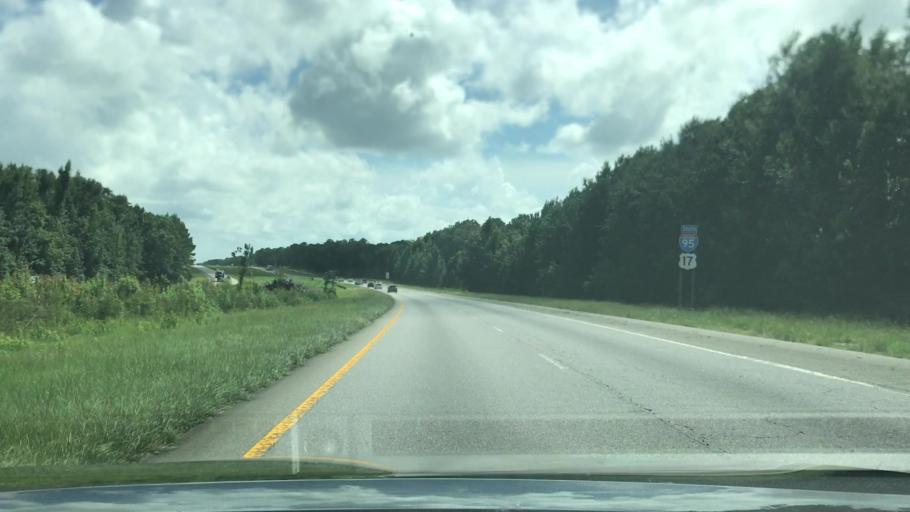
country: US
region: South Carolina
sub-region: Jasper County
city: Ridgeland
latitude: 32.5744
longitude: -80.9363
